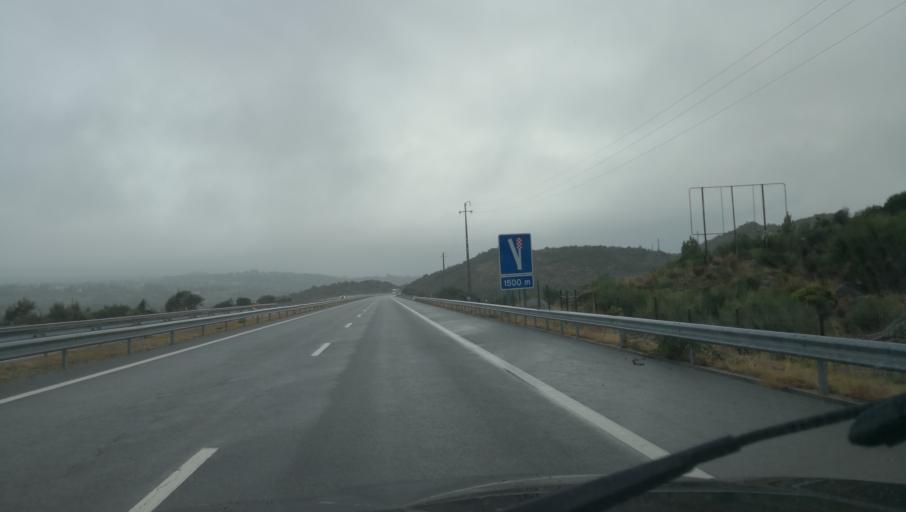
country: PT
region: Vila Real
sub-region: Vila Real
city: Vila Real
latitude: 41.3804
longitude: -7.6664
